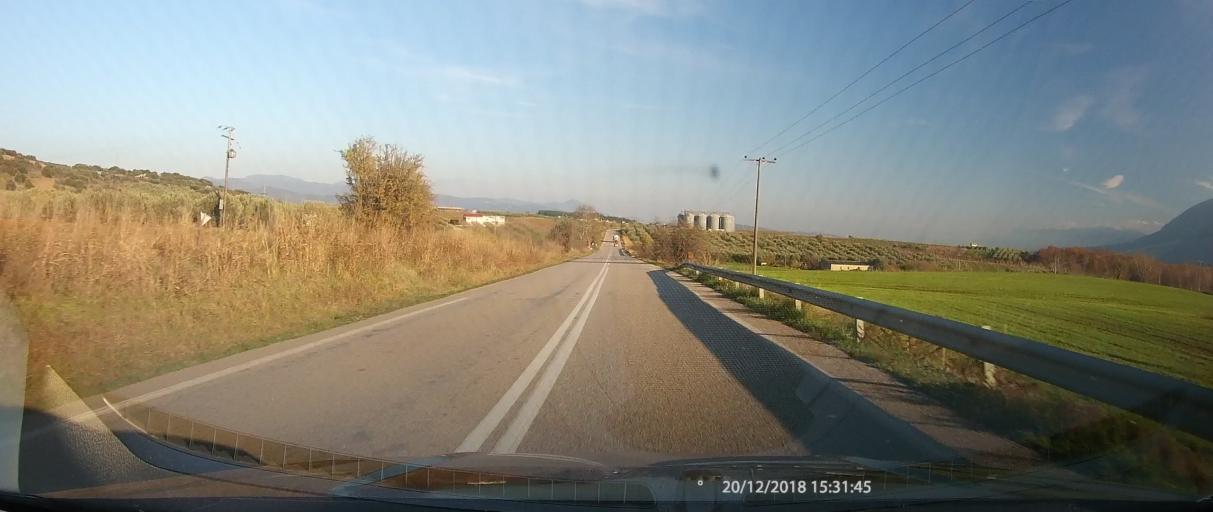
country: GR
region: Central Greece
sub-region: Nomos Fthiotidos
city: Lianokladhion
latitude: 38.9297
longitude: 22.2454
